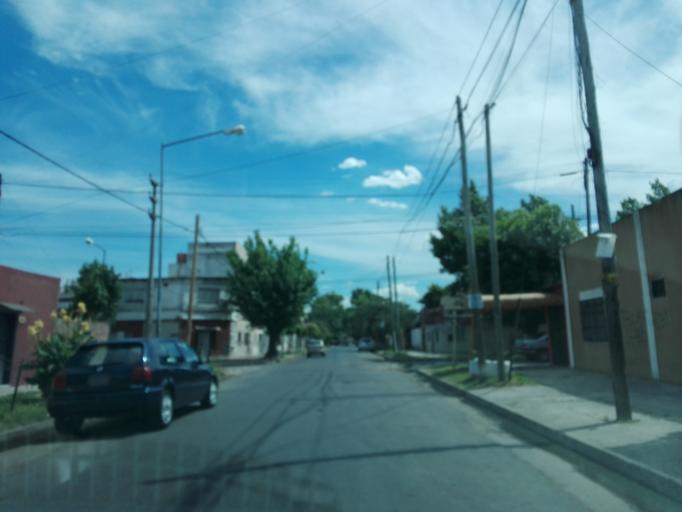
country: AR
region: Buenos Aires
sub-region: Partido de Lanus
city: Lanus
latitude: -34.7224
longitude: -58.3871
